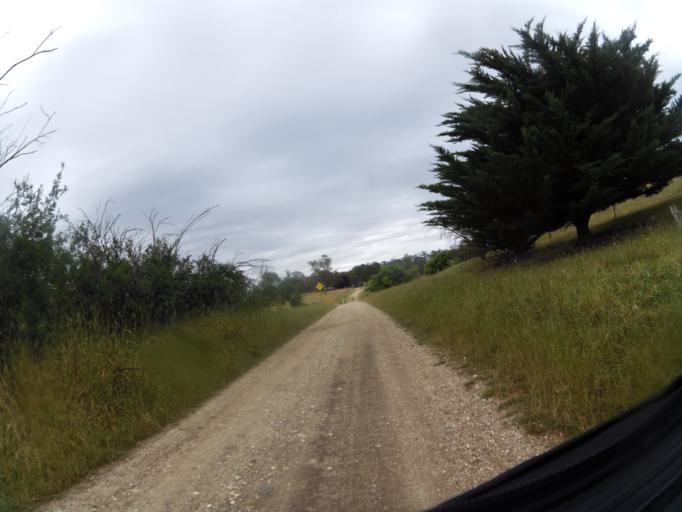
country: AU
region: Victoria
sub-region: Mount Alexander
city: Castlemaine
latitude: -37.2021
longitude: 144.0168
